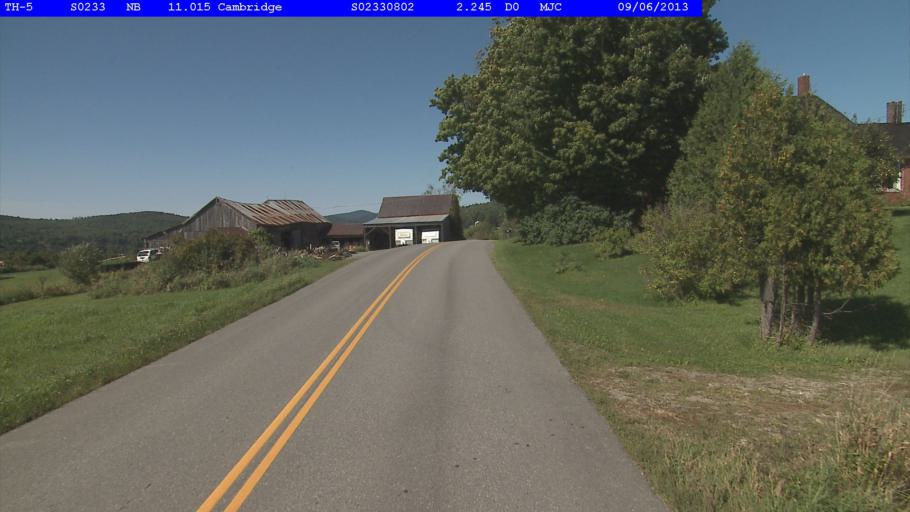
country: US
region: Vermont
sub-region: Chittenden County
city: Jericho
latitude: 44.6140
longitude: -72.8576
